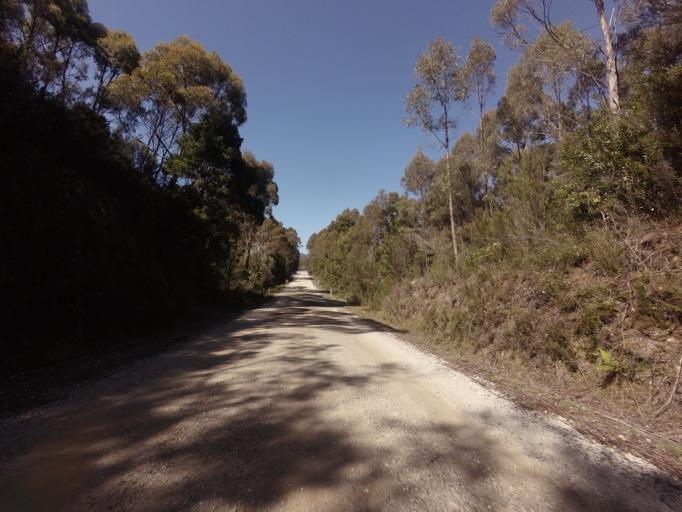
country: AU
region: Tasmania
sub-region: Huon Valley
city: Geeveston
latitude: -43.0107
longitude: 146.3636
